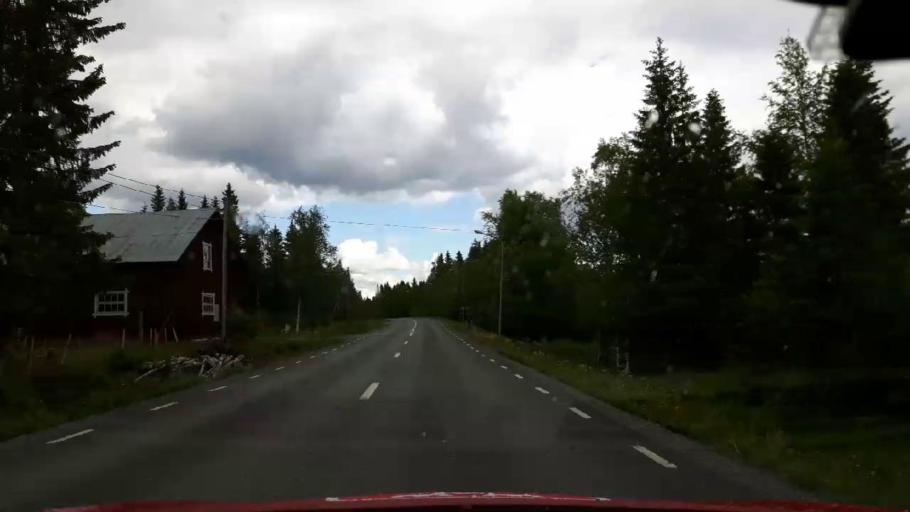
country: SE
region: Jaemtland
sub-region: Krokoms Kommun
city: Krokom
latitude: 63.7506
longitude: 14.2945
